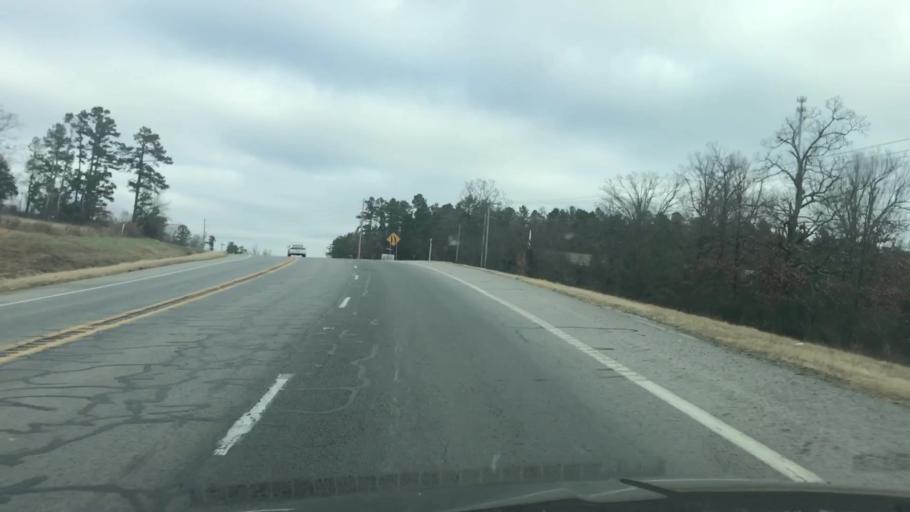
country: US
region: Arkansas
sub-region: Scott County
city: Waldron
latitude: 34.8182
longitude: -94.0374
